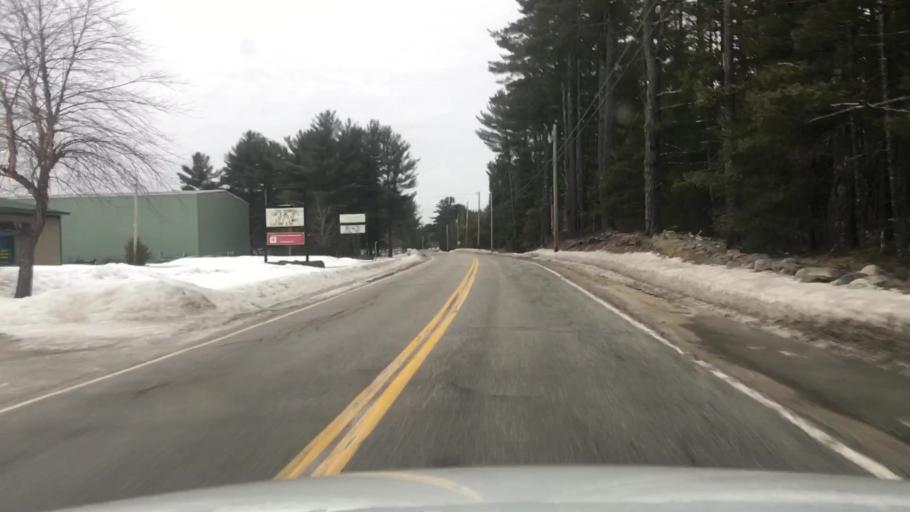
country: US
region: Maine
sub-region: York County
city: Shapleigh
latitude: 43.5617
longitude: -70.8574
